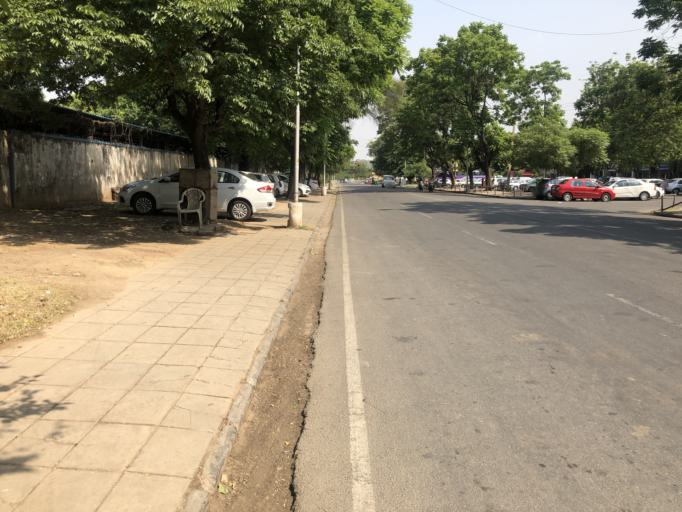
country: IN
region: Chandigarh
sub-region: Chandigarh
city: Chandigarh
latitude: 30.6945
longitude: 76.7712
